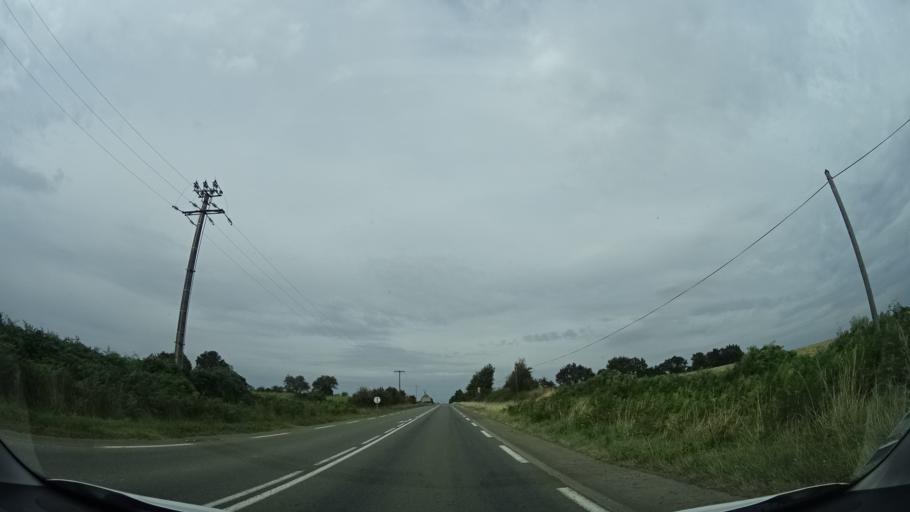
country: FR
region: Pays de la Loire
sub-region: Departement de la Sarthe
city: Auvers-le-Hamon
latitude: 47.8786
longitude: -0.3987
